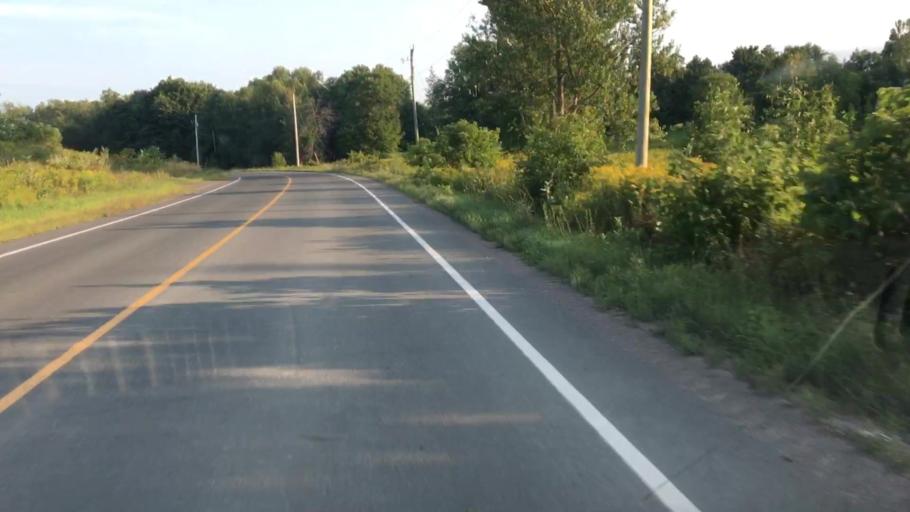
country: CA
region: Ontario
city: Quinte West
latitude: 44.0969
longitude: -77.7354
